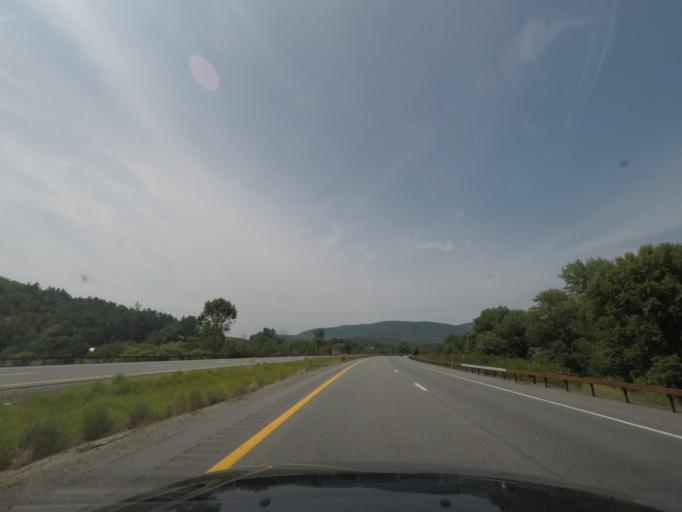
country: US
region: New York
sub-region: Warren County
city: Warrensburg
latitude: 43.7249
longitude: -73.8224
